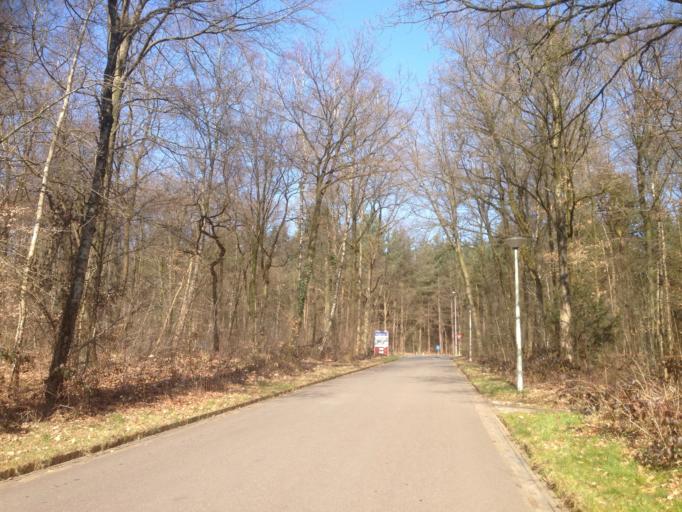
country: NL
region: Gelderland
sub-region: Gemeente Overbetuwe
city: Randwijk
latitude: 51.9668
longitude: 5.7017
